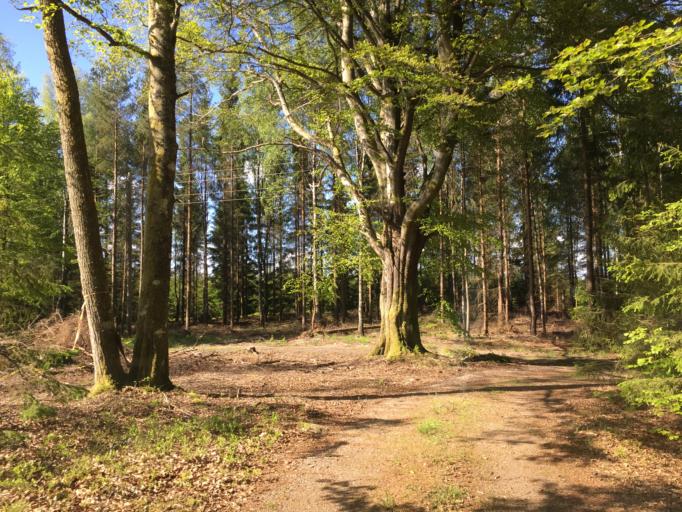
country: SE
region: Kronoberg
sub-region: Markaryds Kommun
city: Markaryd
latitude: 56.5172
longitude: 13.6064
